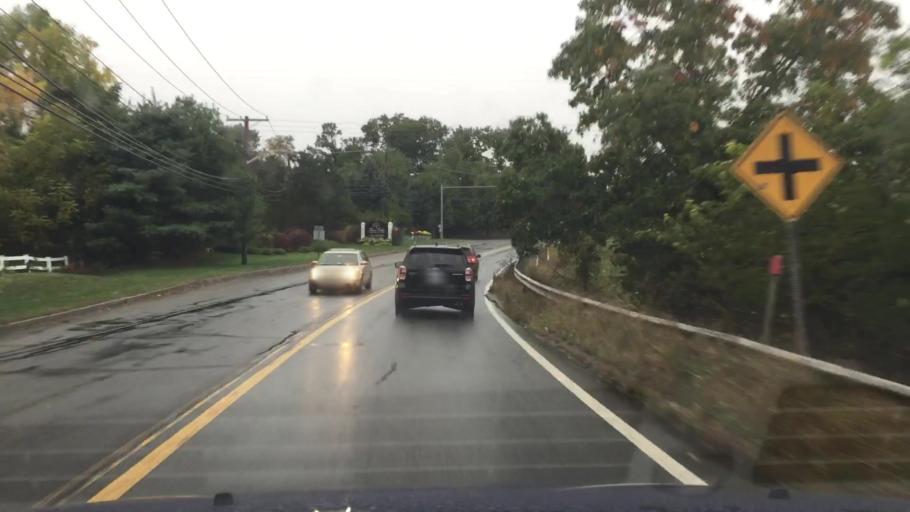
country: US
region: Massachusetts
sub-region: Middlesex County
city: Dracut
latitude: 42.6782
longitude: -71.2941
